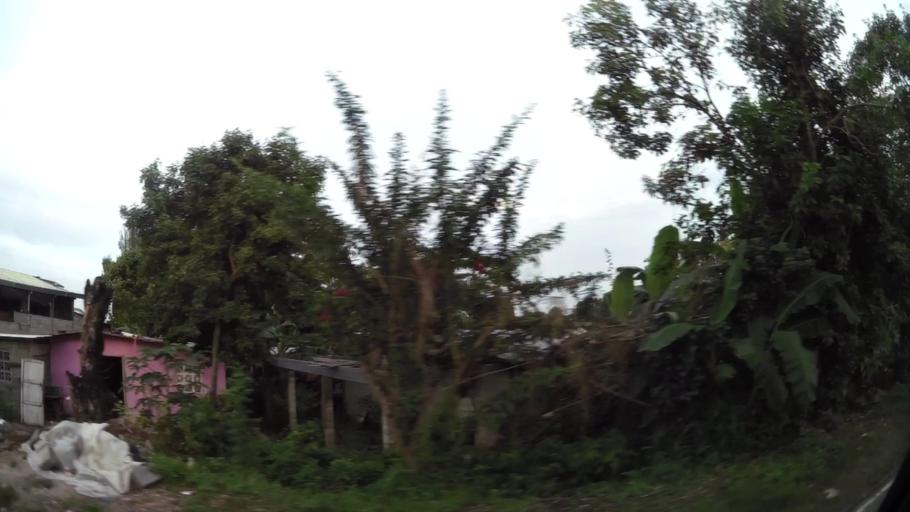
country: PA
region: Panama
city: Tocumen
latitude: 9.0901
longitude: -79.3898
